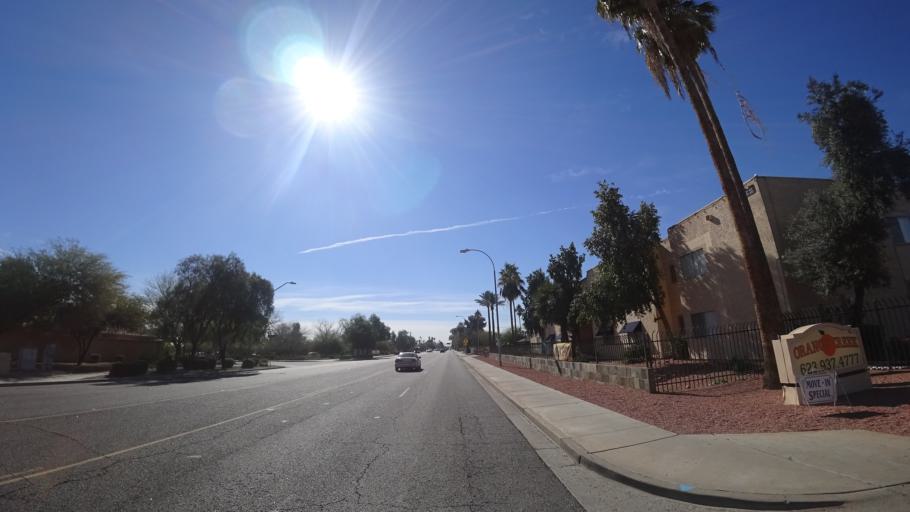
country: US
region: Arizona
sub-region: Maricopa County
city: Glendale
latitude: 33.5621
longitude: -112.1864
